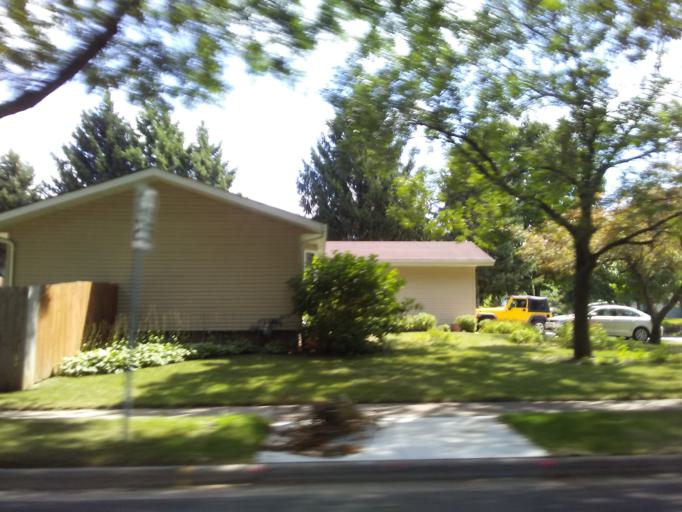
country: US
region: Wisconsin
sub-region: Dane County
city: Verona
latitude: 43.0199
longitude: -89.5032
